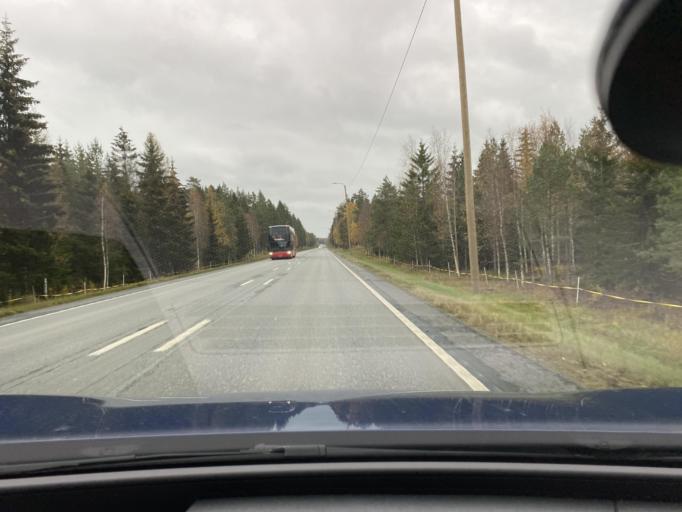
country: FI
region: Varsinais-Suomi
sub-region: Vakka-Suomi
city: Laitila
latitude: 60.9516
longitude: 21.5981
